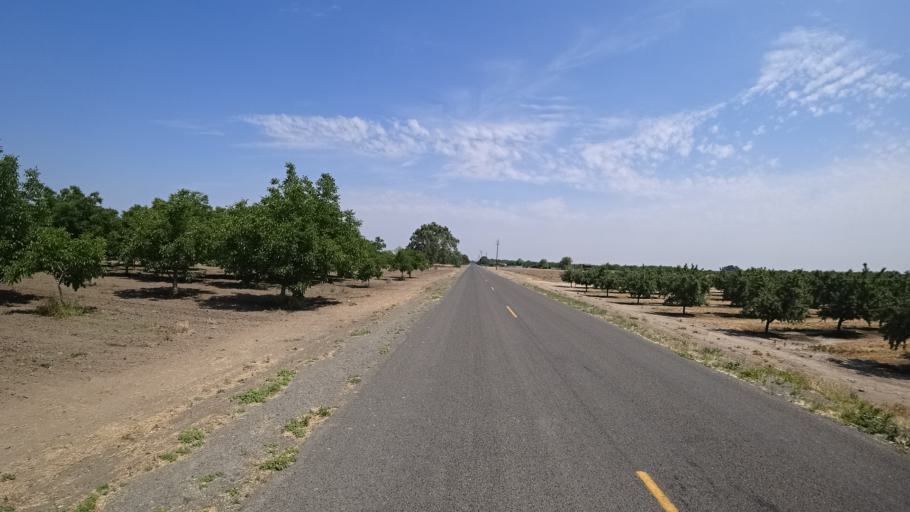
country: US
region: California
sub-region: Fresno County
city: Laton
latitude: 36.3923
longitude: -119.7450
